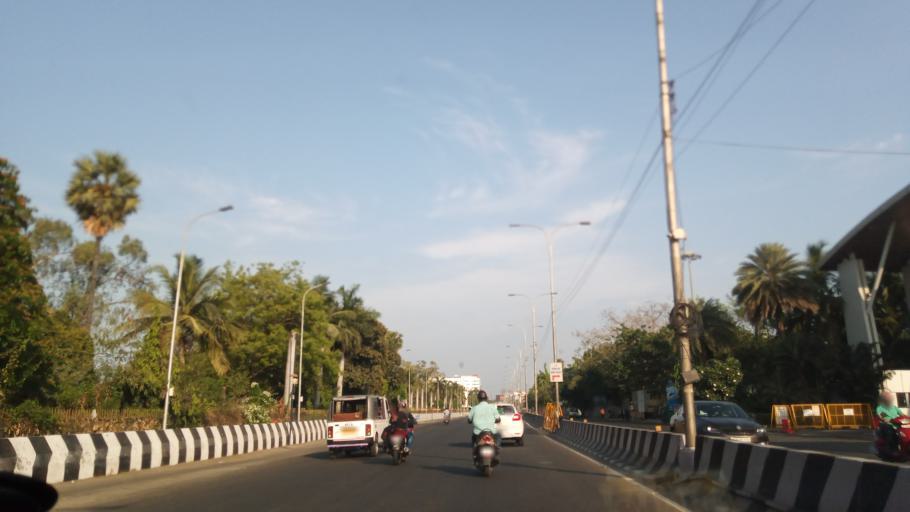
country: IN
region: Tamil Nadu
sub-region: Kancheepuram
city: Manappakkam
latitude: 13.0248
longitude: 80.1771
